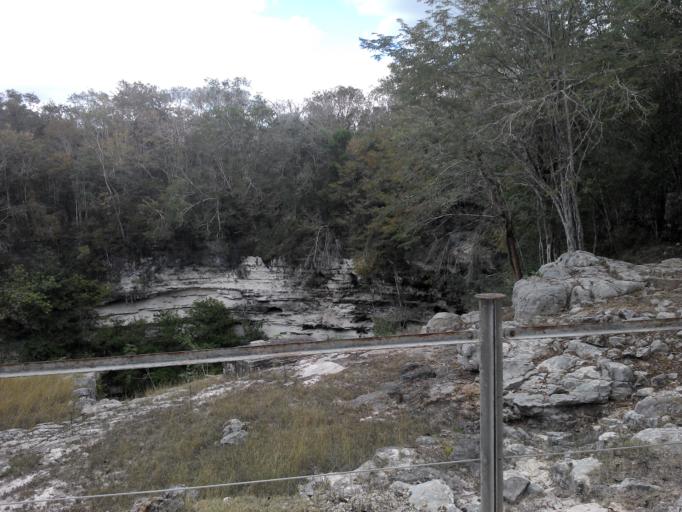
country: MX
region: Yucatan
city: Chichen-Itza
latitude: 20.6874
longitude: -88.5677
